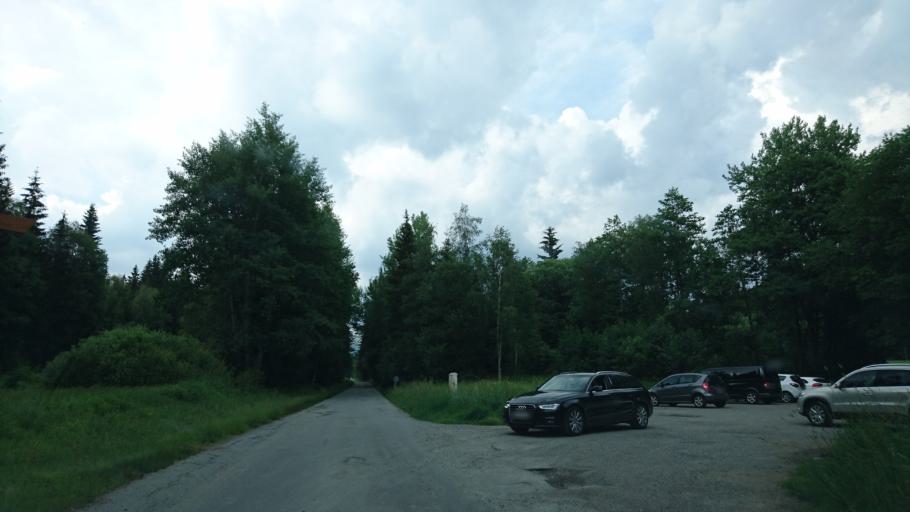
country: DE
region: Bavaria
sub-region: Lower Bavaria
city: Spiegelau
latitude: 48.9217
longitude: 13.3519
